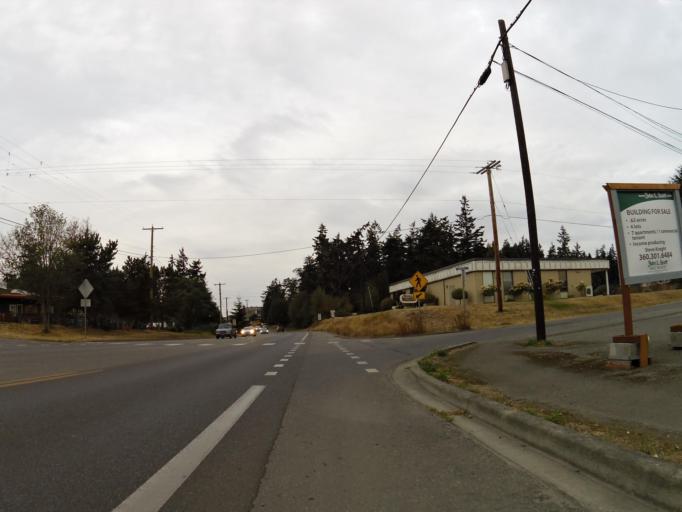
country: US
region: Washington
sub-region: Jefferson County
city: Port Townsend
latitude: 48.1034
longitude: -122.7944
